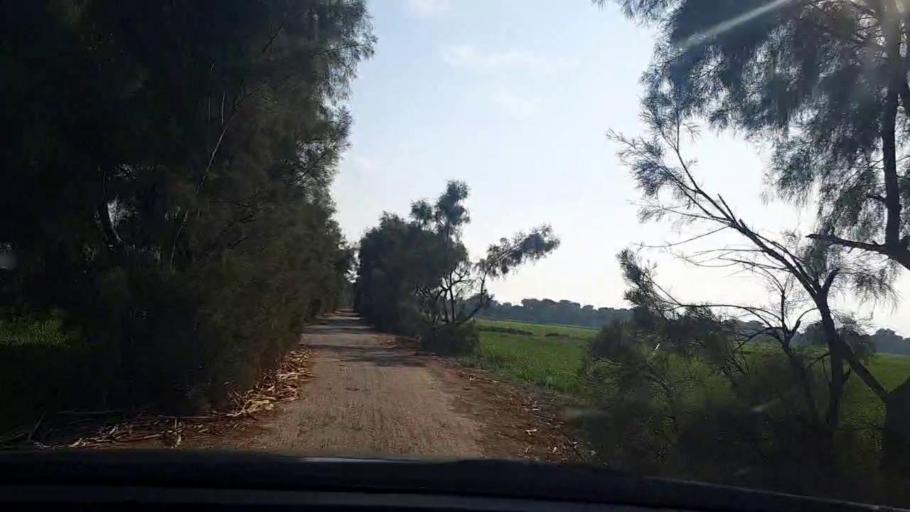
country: PK
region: Sindh
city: Sehwan
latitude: 26.3024
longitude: 68.0047
